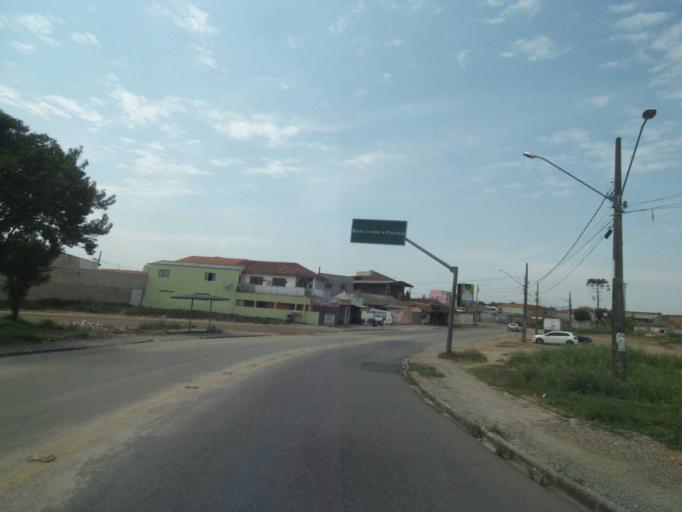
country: BR
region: Parana
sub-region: Pinhais
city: Pinhais
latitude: -25.4223
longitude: -49.1978
